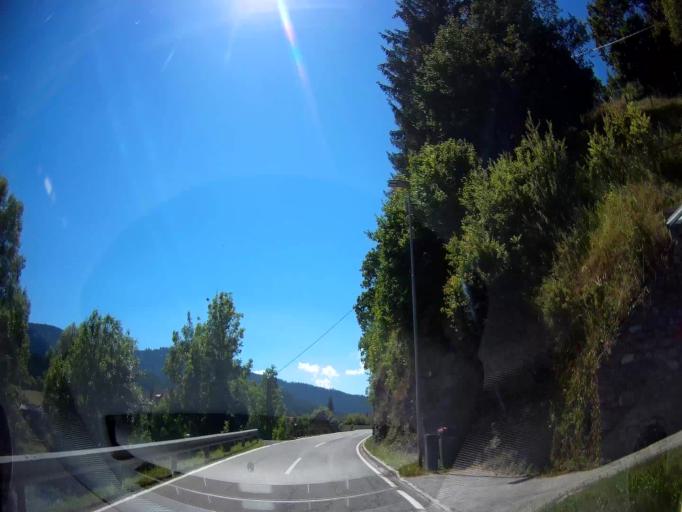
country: AT
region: Carinthia
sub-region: Politischer Bezirk Sankt Veit an der Glan
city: Glodnitz
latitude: 46.8501
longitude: 14.1959
